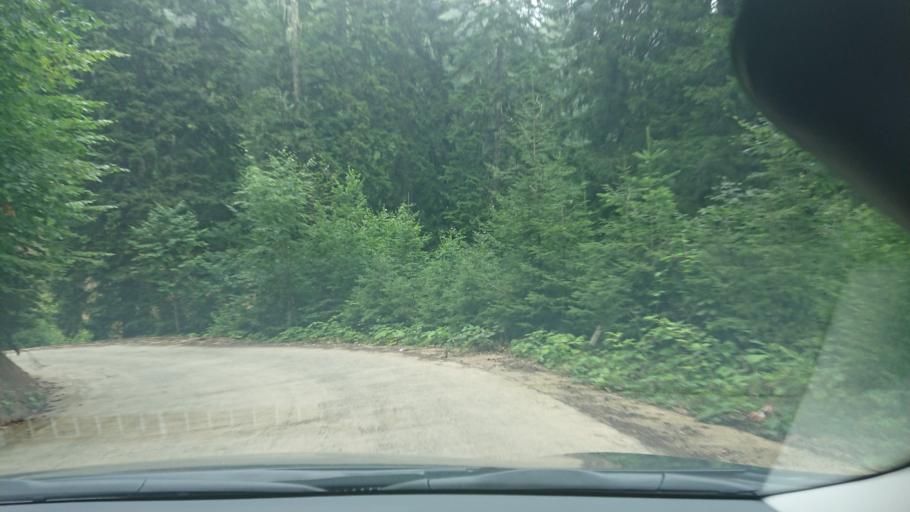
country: TR
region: Gumushane
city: Kurtun
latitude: 40.6583
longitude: 39.0200
